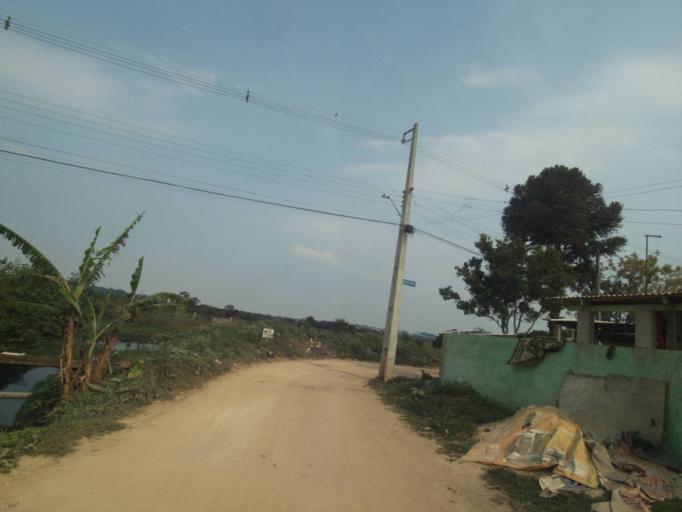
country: BR
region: Parana
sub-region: Sao Jose Dos Pinhais
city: Sao Jose dos Pinhais
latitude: -25.5393
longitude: -49.2319
